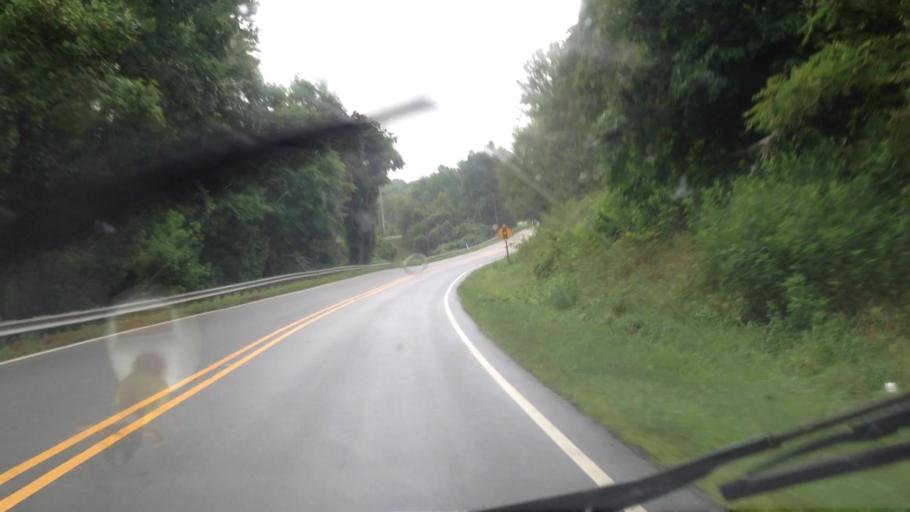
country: US
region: North Carolina
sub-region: Rockingham County
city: Mayodan
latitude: 36.4054
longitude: -79.9833
